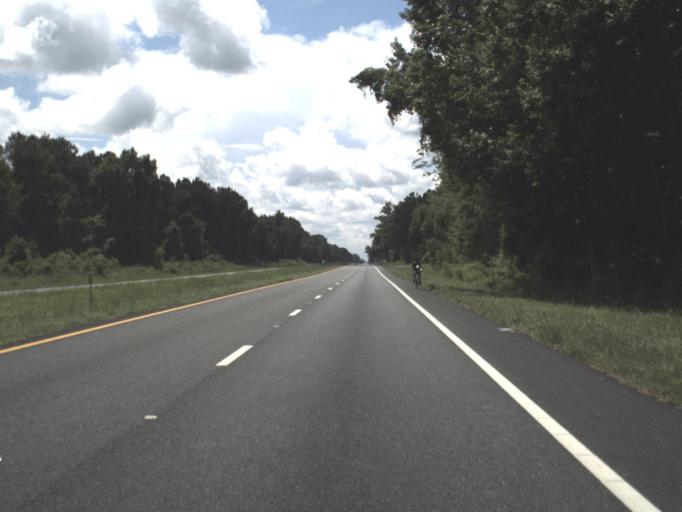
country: US
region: Florida
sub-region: Taylor County
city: Perry
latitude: 30.3061
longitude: -83.7508
